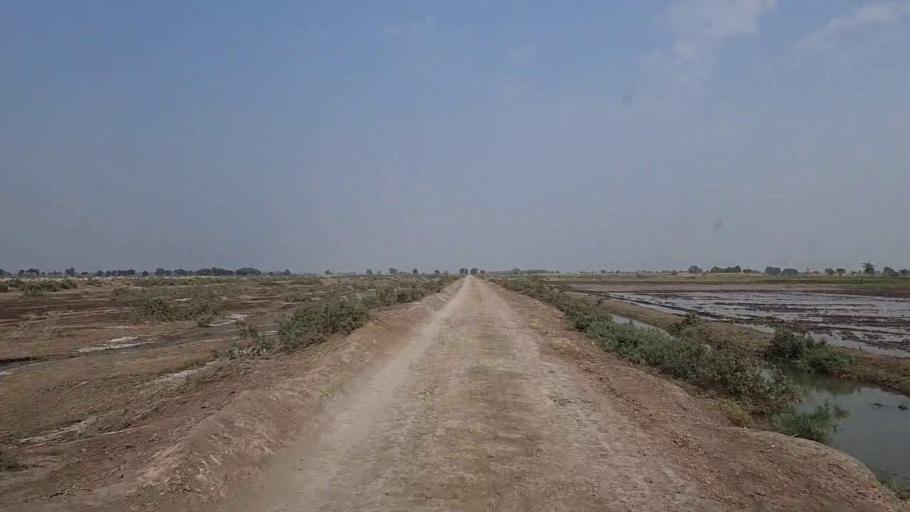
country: PK
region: Sindh
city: Mirwah Gorchani
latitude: 25.3808
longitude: 69.0483
